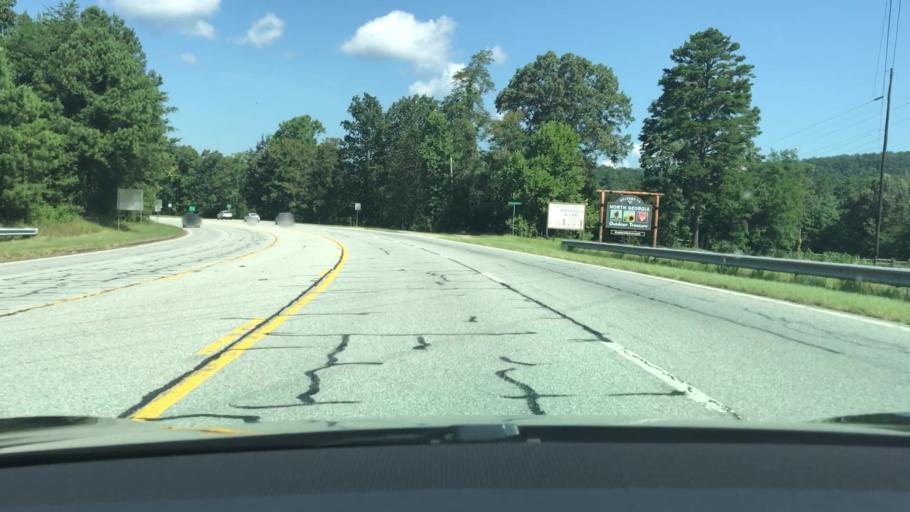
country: US
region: Georgia
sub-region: Rabun County
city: Clayton
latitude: 34.7348
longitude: -83.3894
